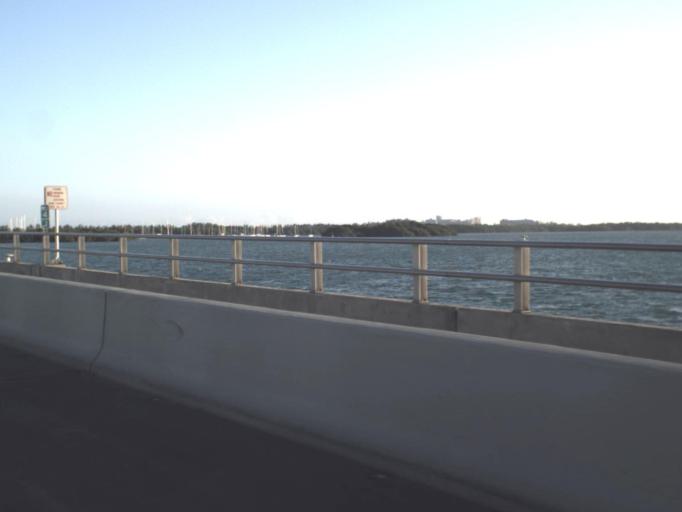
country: US
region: Florida
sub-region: Miami-Dade County
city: Key Biscayne
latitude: 25.7321
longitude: -80.1607
